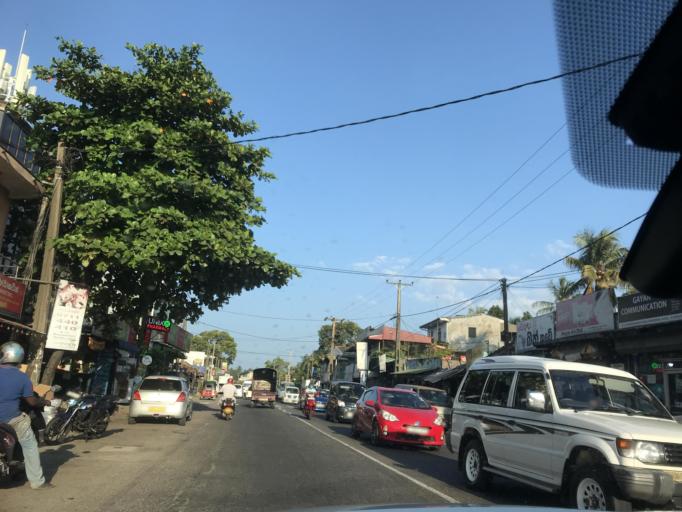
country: LK
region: Western
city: Ja Ela
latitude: 7.0850
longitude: 79.8936
